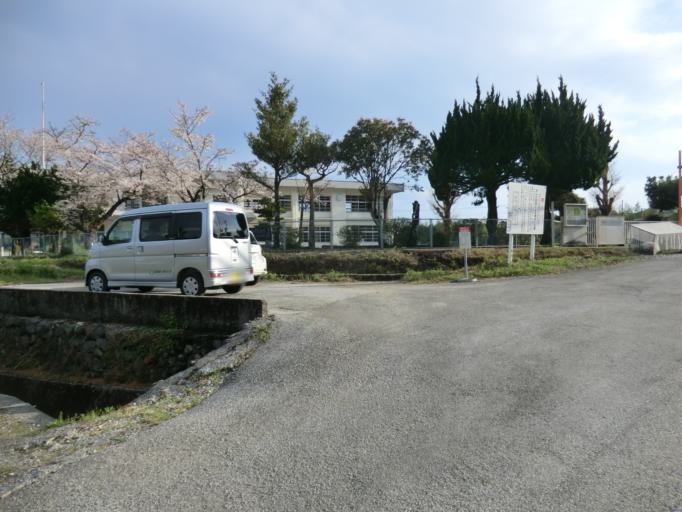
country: JP
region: Kochi
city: Kochi-shi
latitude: 33.6392
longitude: 133.7184
